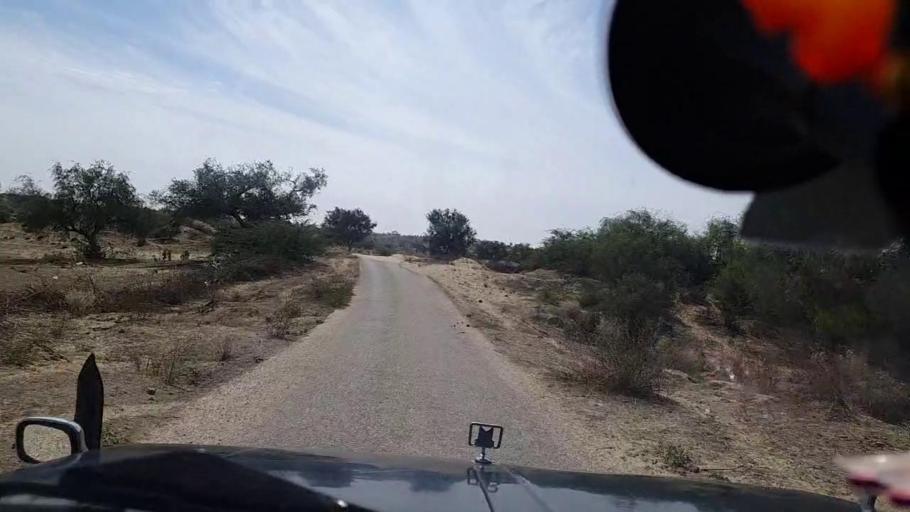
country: PK
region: Sindh
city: Diplo
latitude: 24.3927
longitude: 69.5882
